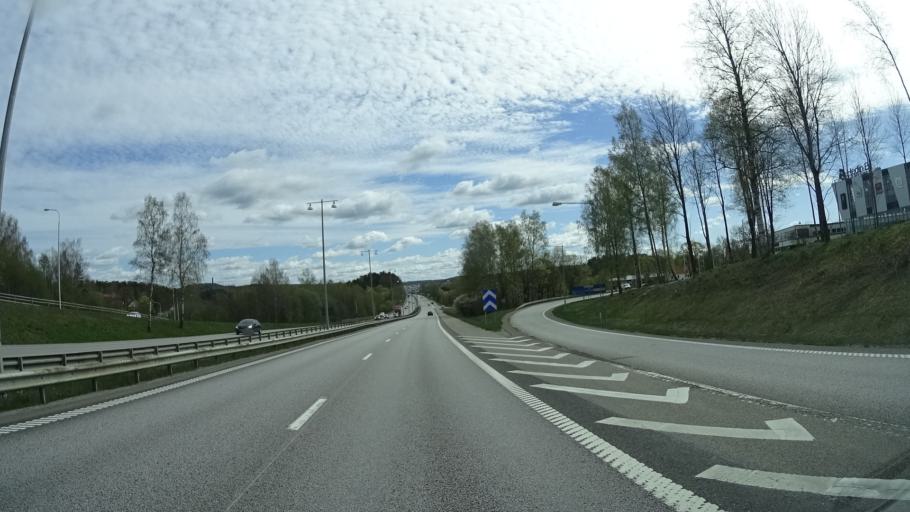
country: SE
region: Vaestra Goetaland
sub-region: Boras Kommun
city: Boras
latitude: 57.7162
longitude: 12.9100
